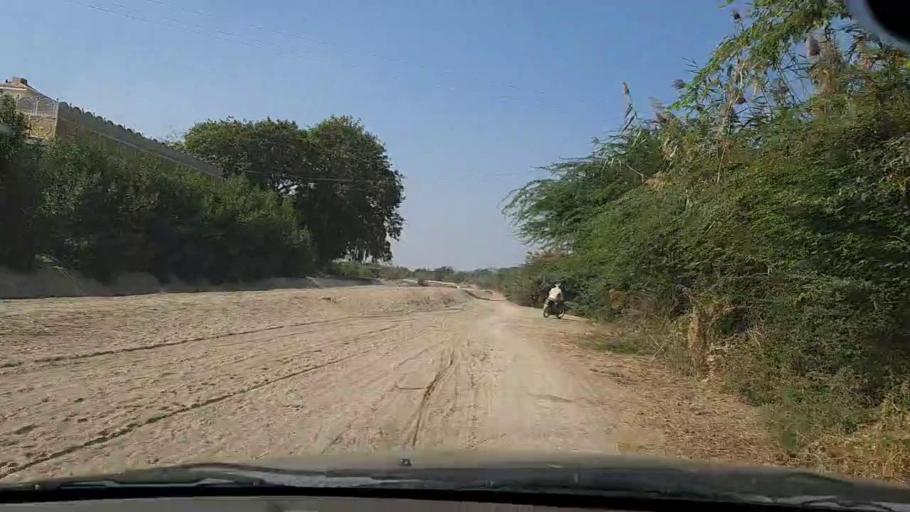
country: PK
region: Sindh
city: Chuhar Jamali
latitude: 24.4265
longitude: 67.8133
